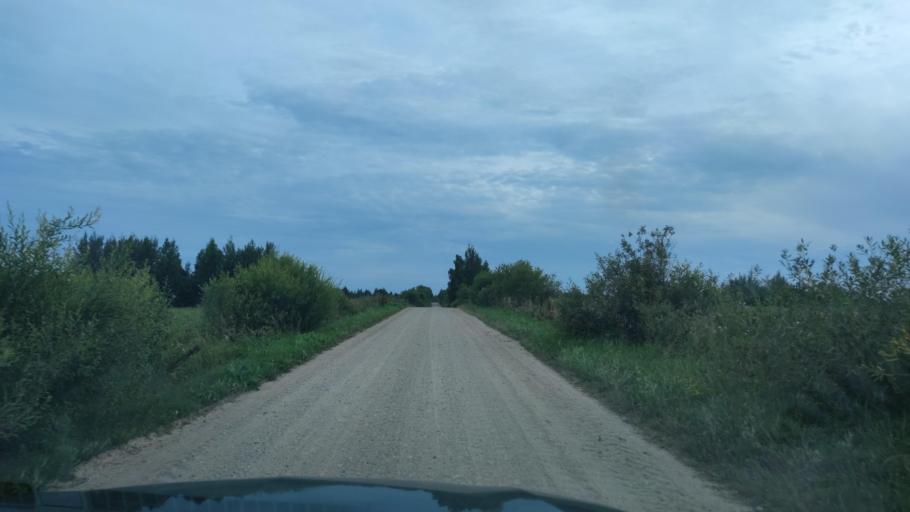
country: BY
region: Vitebsk
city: Mosar
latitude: 55.1254
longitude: 27.1570
